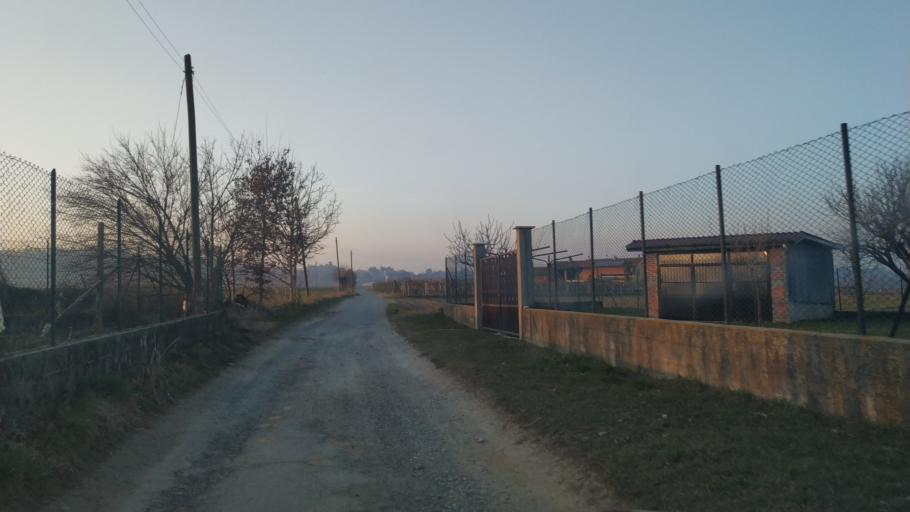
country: IT
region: Piedmont
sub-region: Provincia di Vercelli
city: Cigliano
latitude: 45.3160
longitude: 8.0140
